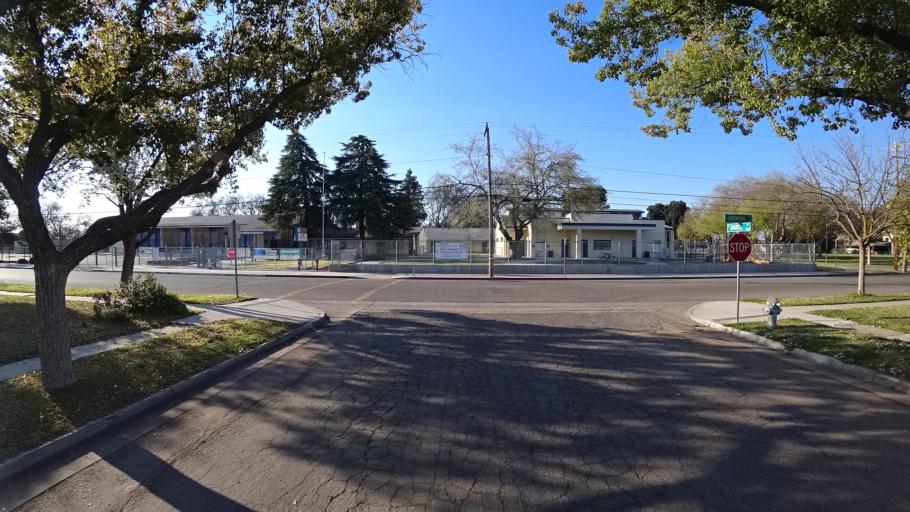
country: US
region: California
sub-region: Fresno County
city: Fresno
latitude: 36.8195
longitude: -119.7788
